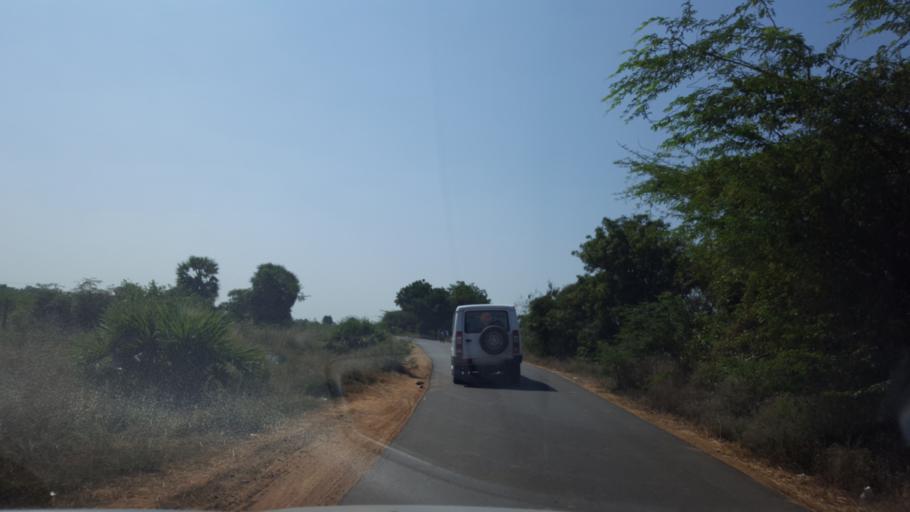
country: IN
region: Tamil Nadu
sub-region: Kancheepuram
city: Wallajahbad
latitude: 12.8599
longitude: 79.7906
